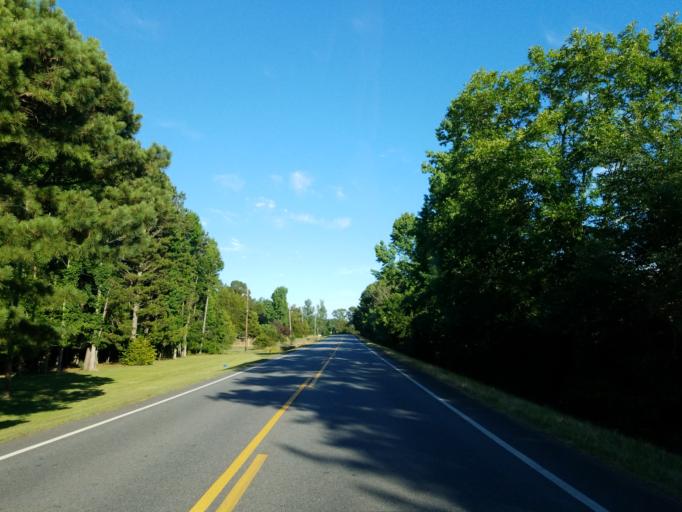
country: US
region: Georgia
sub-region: Gordon County
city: Calhoun
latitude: 34.5430
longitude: -85.0000
